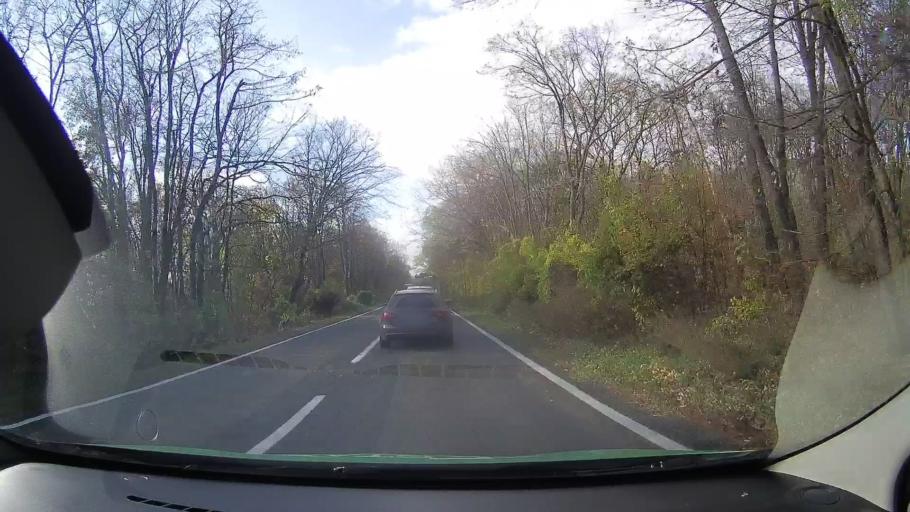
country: RO
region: Tulcea
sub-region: Comuna Topolog
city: Topolog
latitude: 44.9068
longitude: 28.4134
